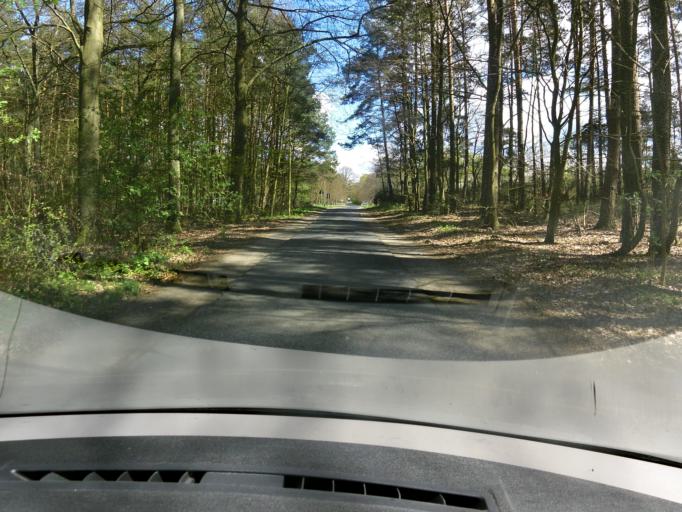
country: DE
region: Mecklenburg-Vorpommern
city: Malchow
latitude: 53.4585
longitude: 12.3664
